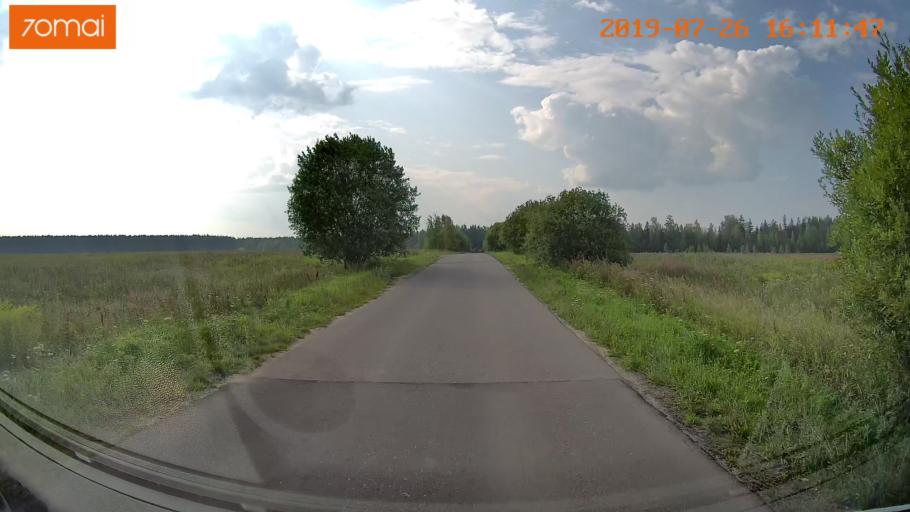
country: RU
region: Ivanovo
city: Bogorodskoye
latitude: 57.0669
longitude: 41.0555
